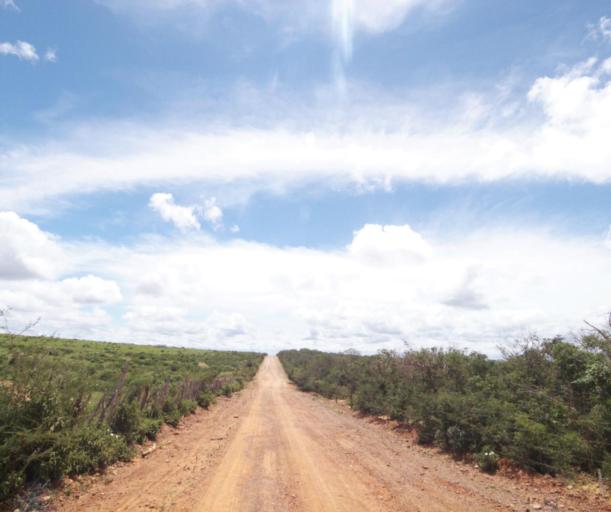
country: BR
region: Bahia
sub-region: Tanhacu
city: Tanhacu
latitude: -14.1928
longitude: -41.0539
